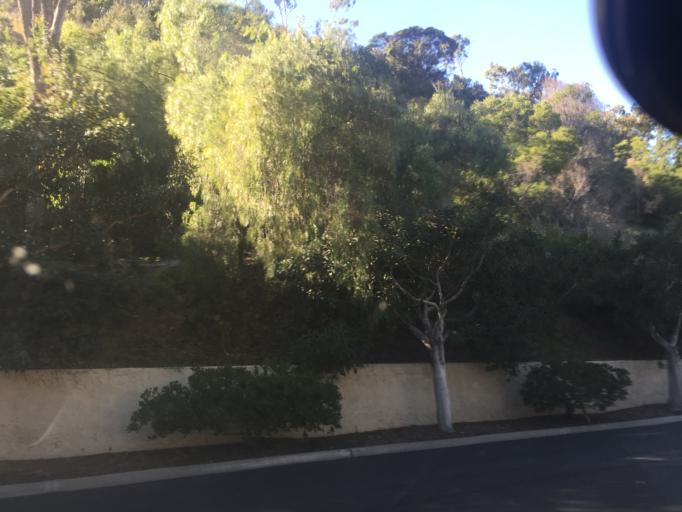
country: US
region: California
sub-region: San Diego County
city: Lemon Grove
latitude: 32.7752
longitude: -117.1007
